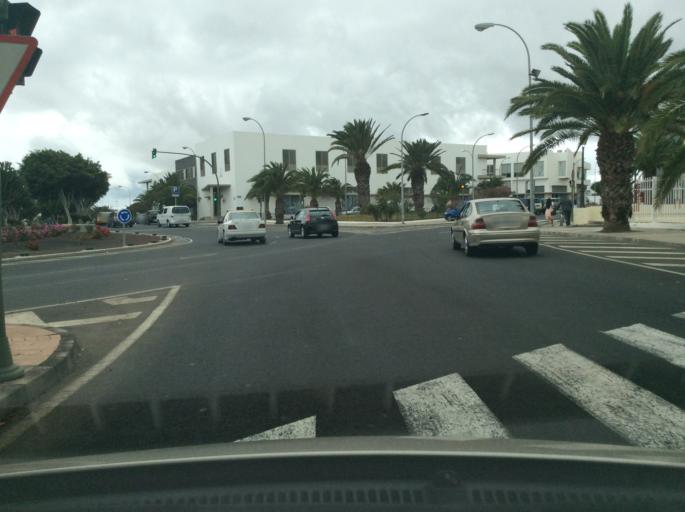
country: ES
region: Canary Islands
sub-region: Provincia de Las Palmas
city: Arrecife
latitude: 28.9661
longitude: -13.5572
